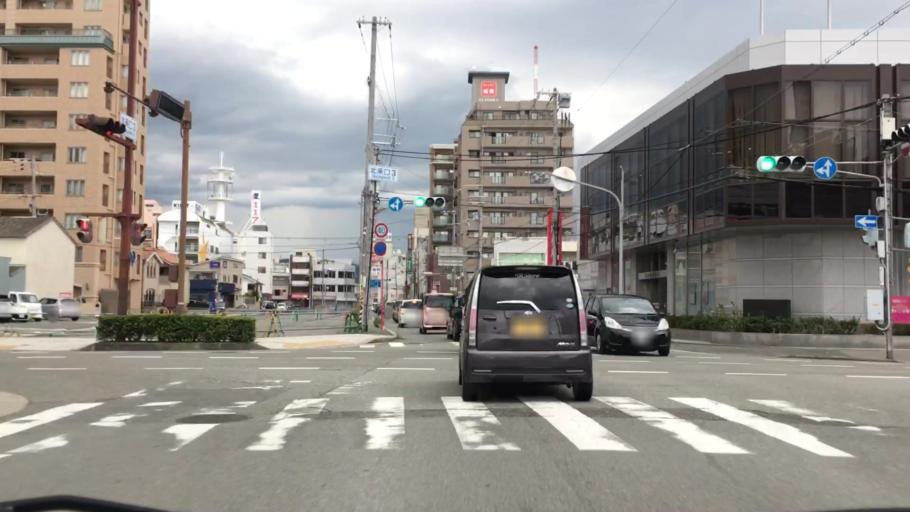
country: JP
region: Hyogo
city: Himeji
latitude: 34.8282
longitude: 134.6963
